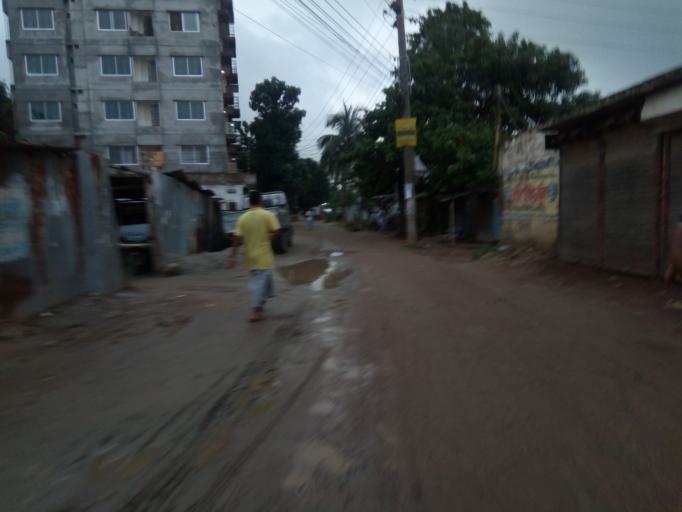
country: BD
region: Dhaka
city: Tungi
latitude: 23.8527
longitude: 90.4323
